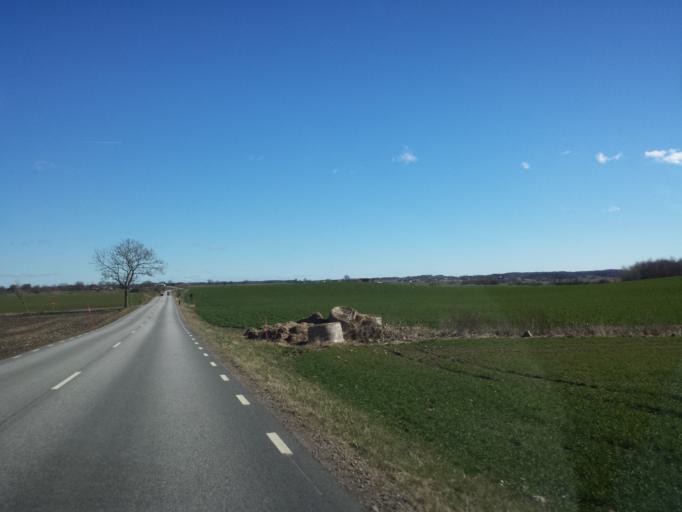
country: SE
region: Skane
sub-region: Tomelilla Kommun
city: Tomelilla
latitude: 55.6274
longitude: 13.8601
